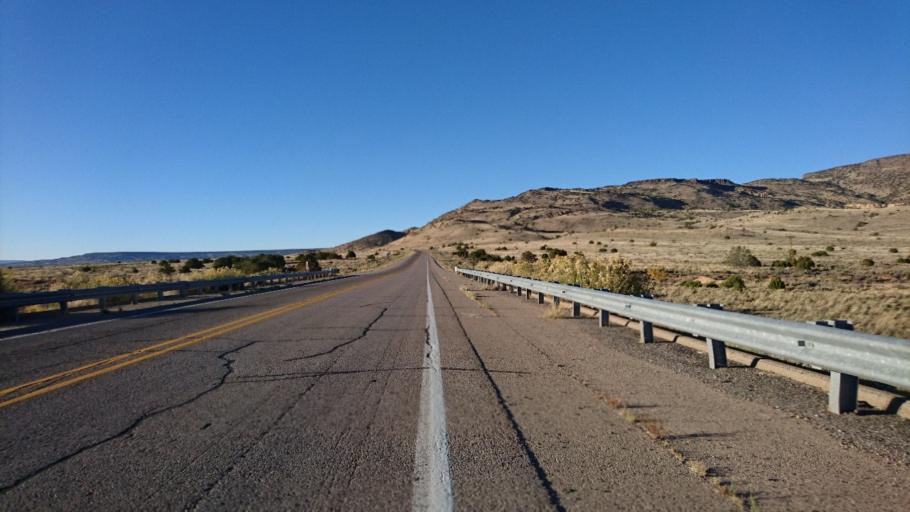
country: US
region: New Mexico
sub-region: Cibola County
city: Grants
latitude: 35.1076
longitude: -107.7805
